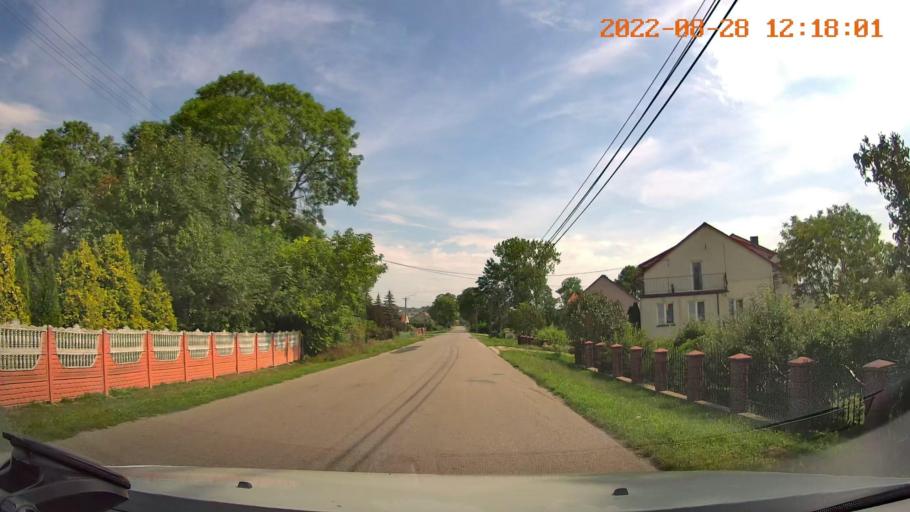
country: PL
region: Swietokrzyskie
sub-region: Powiat pinczowski
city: Zlota
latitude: 50.4475
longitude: 20.5802
